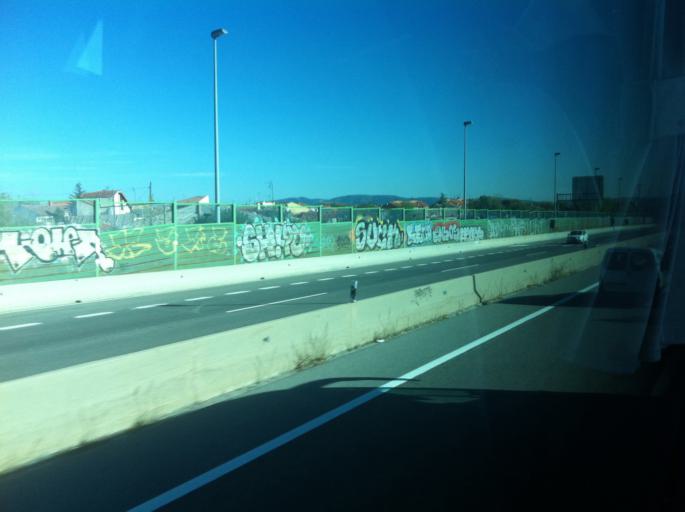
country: ES
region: Madrid
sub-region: Provincia de Madrid
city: Garganta de los Montes
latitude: 40.9263
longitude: -3.6211
